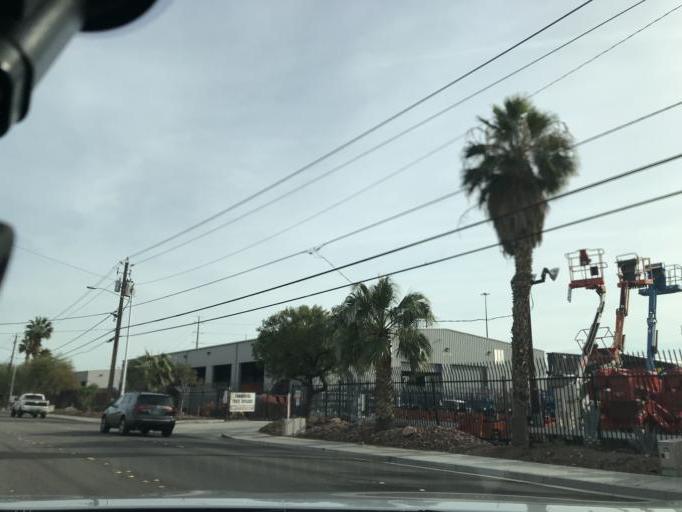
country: US
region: Nevada
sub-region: Clark County
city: Las Vegas
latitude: 36.1772
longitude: -115.1670
